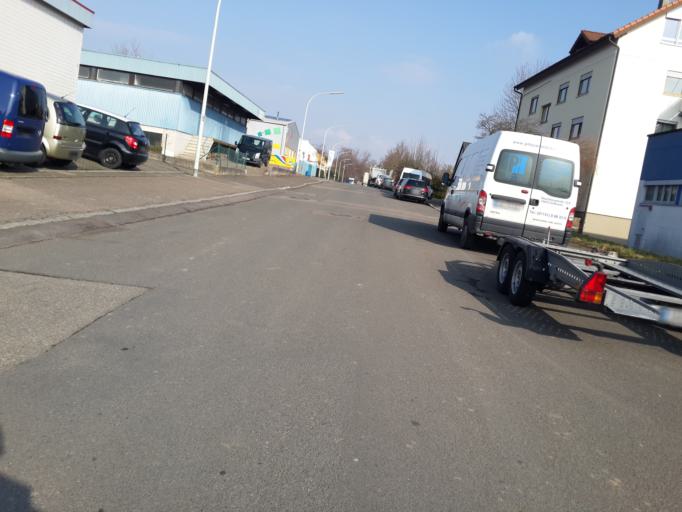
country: DE
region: Baden-Wuerttemberg
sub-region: Regierungsbezirk Stuttgart
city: Heilbronn
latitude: 49.1481
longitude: 9.1943
